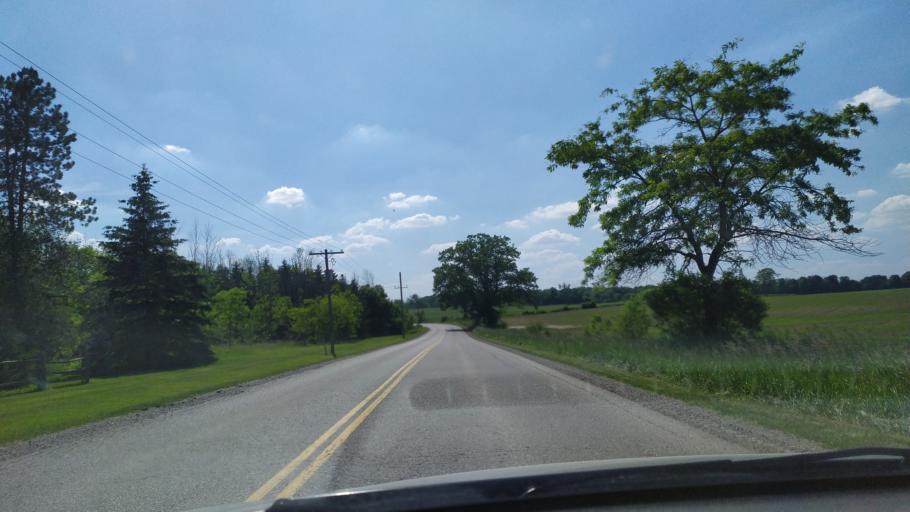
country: CA
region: Ontario
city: Kitchener
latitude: 43.3592
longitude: -80.6409
